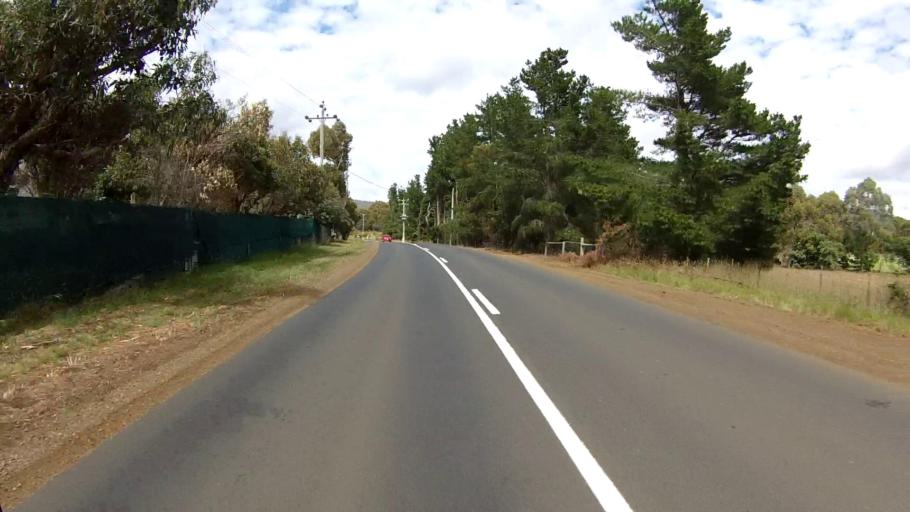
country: AU
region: Tasmania
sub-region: Clarence
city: Cambridge
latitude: -42.7624
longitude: 147.3961
